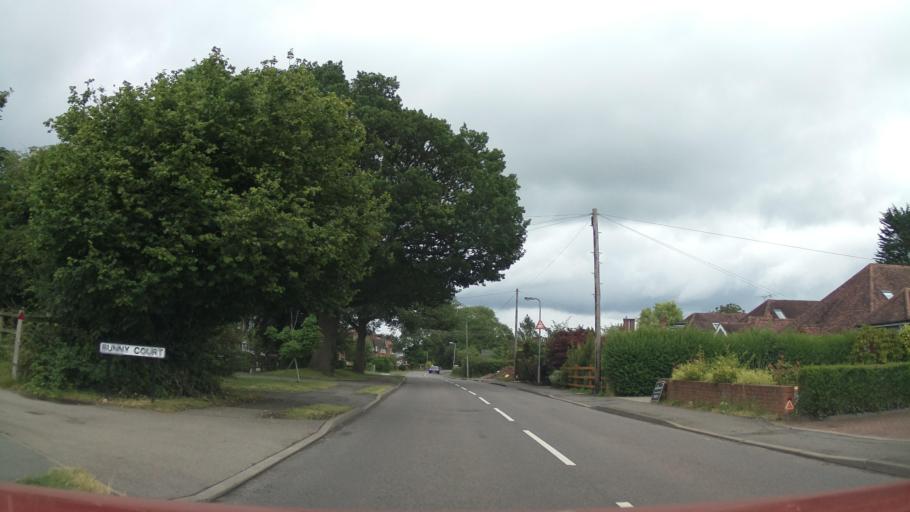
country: GB
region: England
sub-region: Solihull
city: Tidbury Green
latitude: 52.3759
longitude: -1.8745
